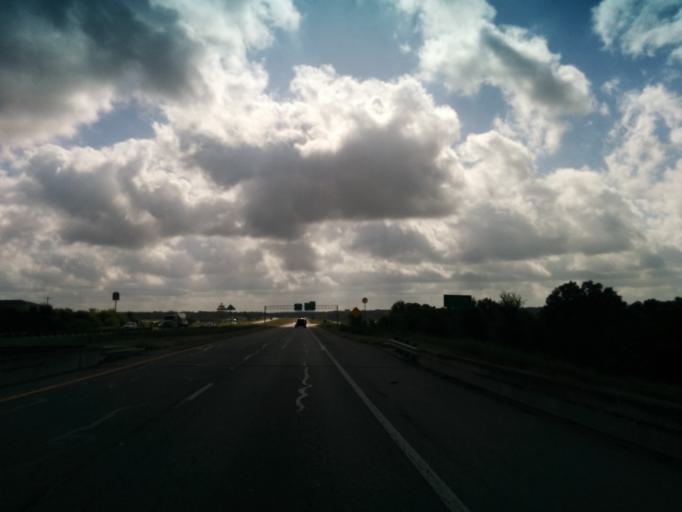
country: US
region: Texas
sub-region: Caldwell County
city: Luling
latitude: 29.6510
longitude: -97.6007
